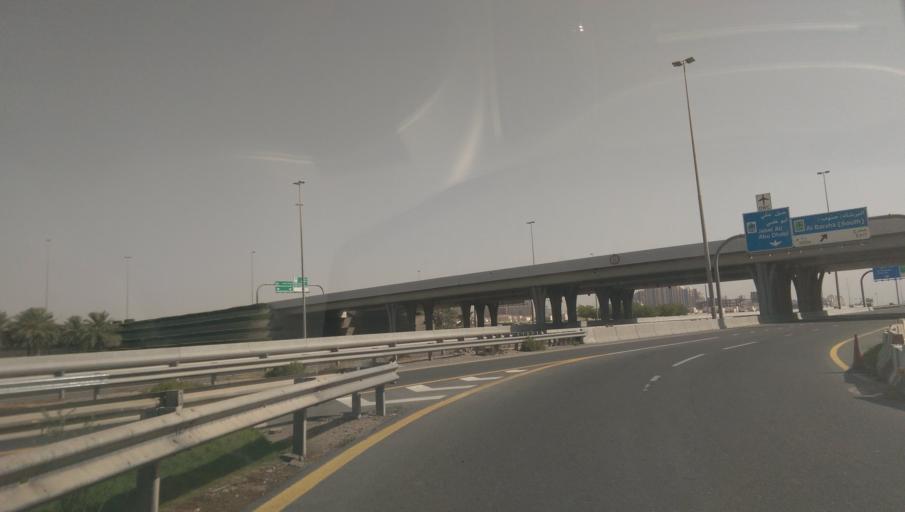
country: AE
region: Dubai
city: Dubai
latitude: 25.0780
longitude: 55.2108
